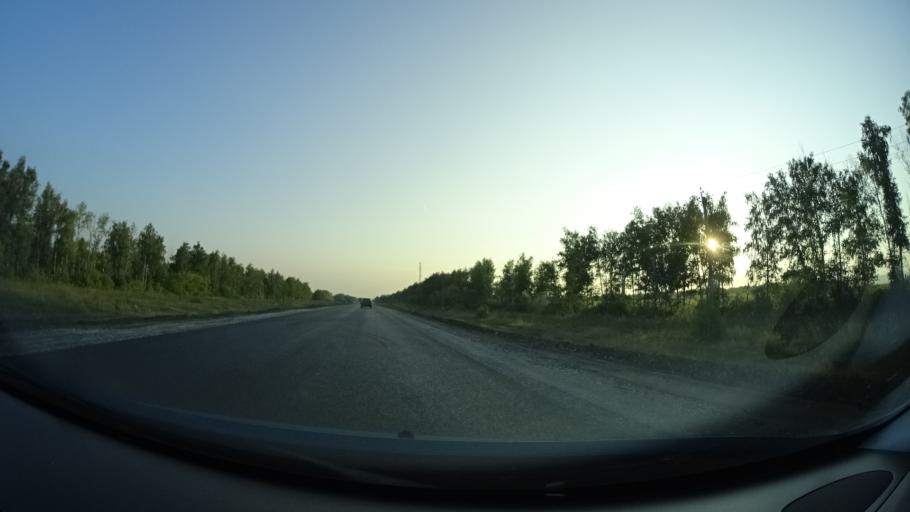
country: RU
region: Samara
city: Isakly
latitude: 53.9815
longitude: 51.4879
